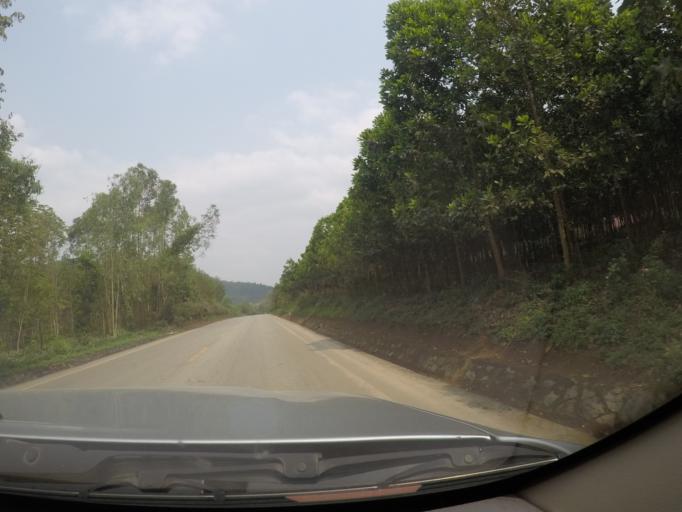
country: VN
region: Thanh Hoa
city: Thi Tran Yen Cat
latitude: 19.4778
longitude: 105.4037
